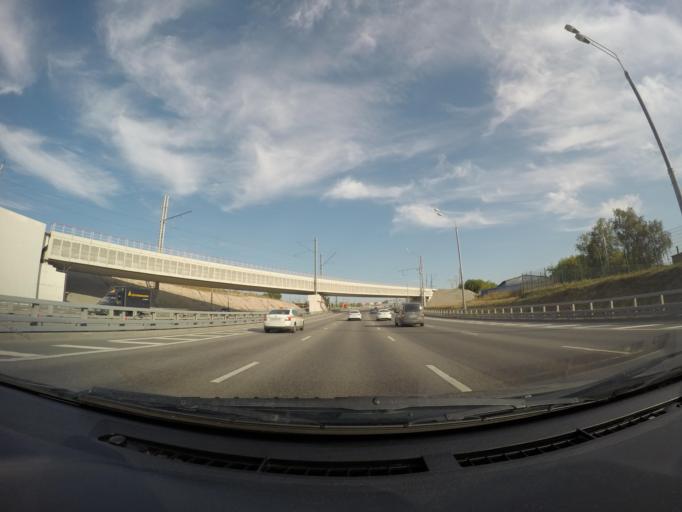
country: RU
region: Moscow
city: Zapadnoye Degunino
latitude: 55.8546
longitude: 37.5420
